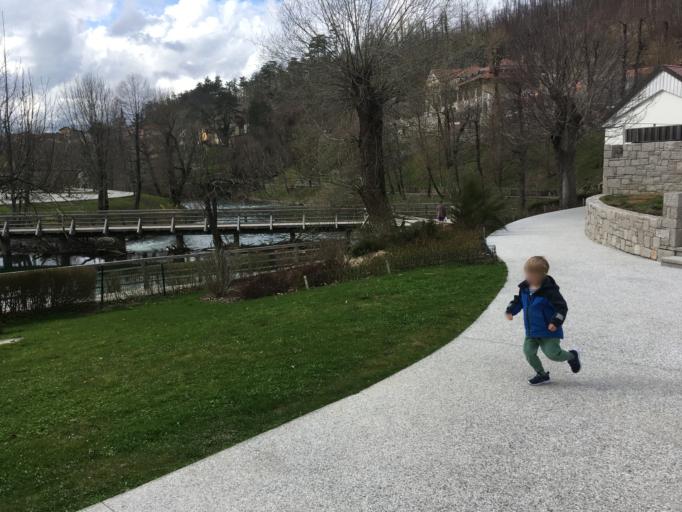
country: SI
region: Postojna
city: Postojna
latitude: 45.7813
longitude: 14.2050
